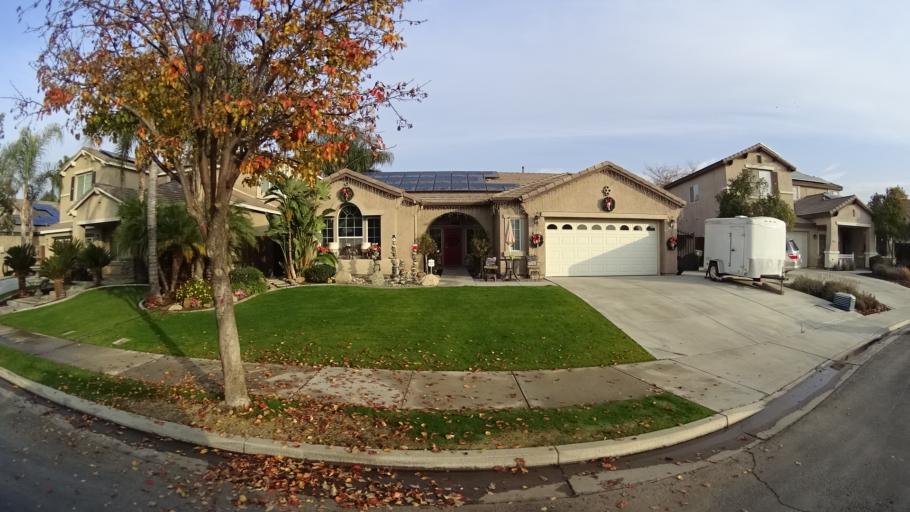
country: US
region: California
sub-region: Kern County
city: Greenacres
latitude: 35.4230
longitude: -119.1215
